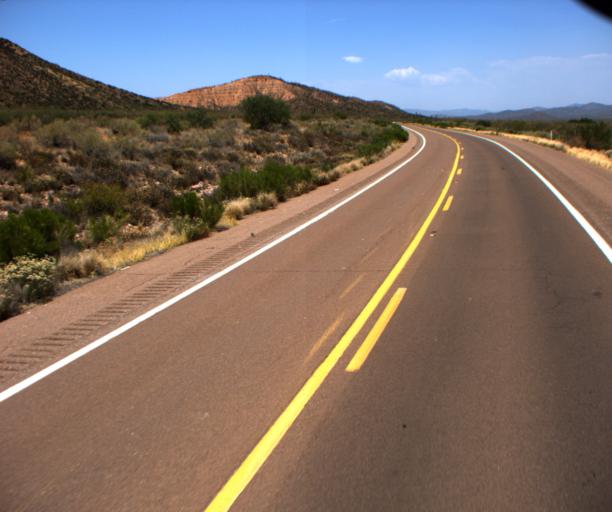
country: US
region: Arizona
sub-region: Gila County
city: Tonto Basin
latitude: 33.8832
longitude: -111.3119
